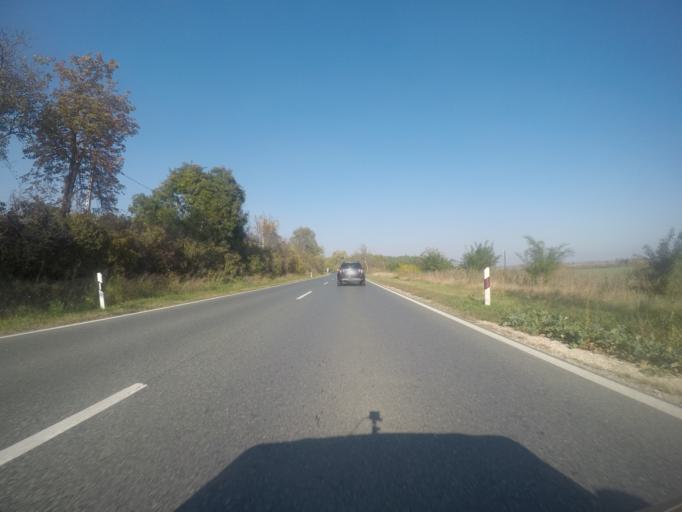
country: HU
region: Tolna
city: Paks
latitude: 46.6830
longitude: 18.8866
